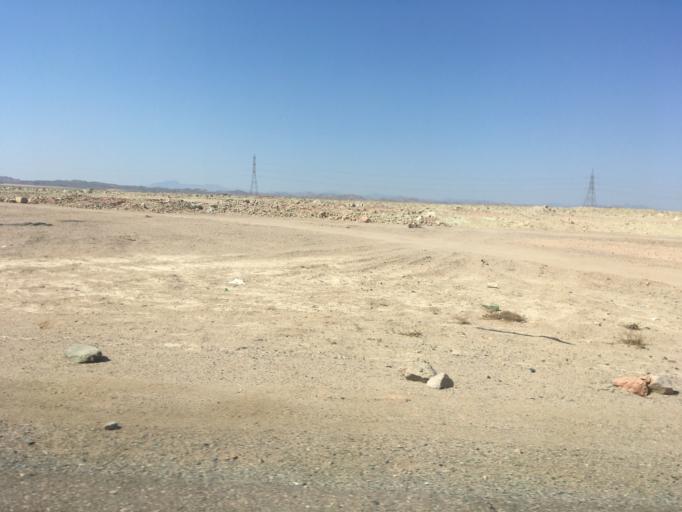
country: EG
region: Red Sea
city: Marsa Alam
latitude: 24.8945
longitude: 34.9709
